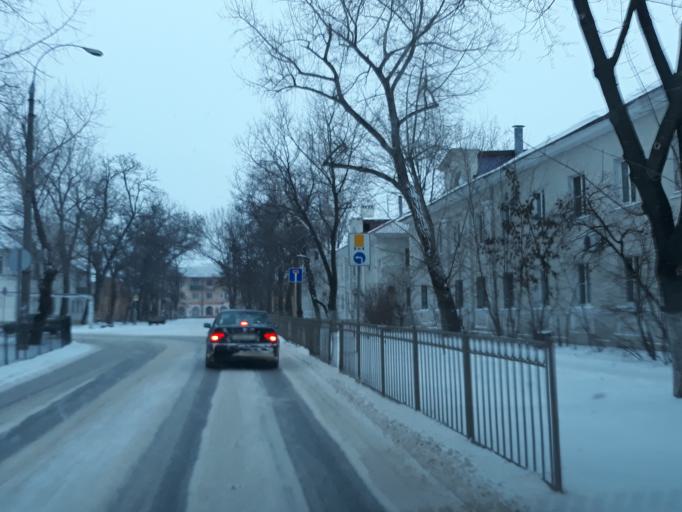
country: RU
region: Rostov
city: Taganrog
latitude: 47.2626
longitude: 38.9382
